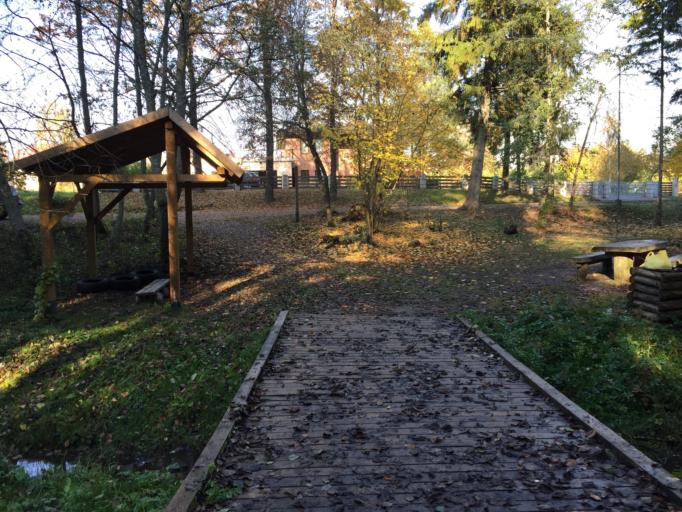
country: LV
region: Saldus Rajons
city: Saldus
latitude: 56.6487
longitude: 22.4877
